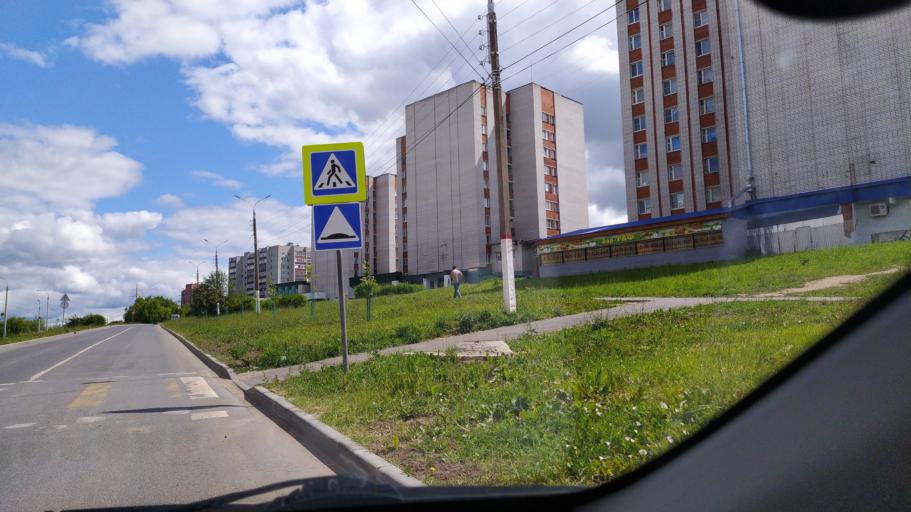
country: RU
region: Chuvashia
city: Novyye Lapsary
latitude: 56.1234
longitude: 47.1828
